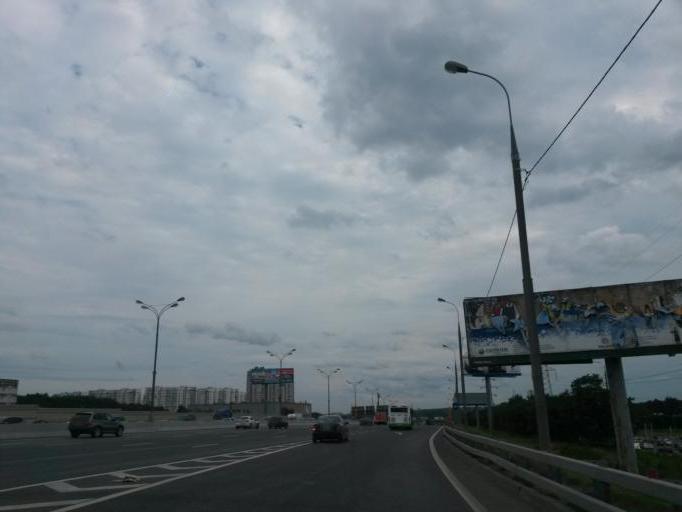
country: RU
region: Moscow
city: Tyoply Stan
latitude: 55.6043
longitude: 37.4994
